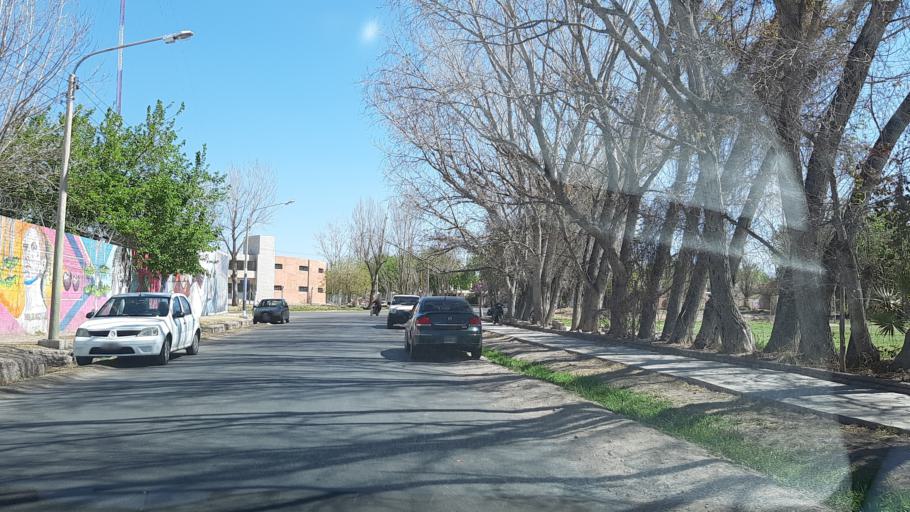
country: AR
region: San Juan
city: San Juan
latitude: -31.5263
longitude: -68.5427
